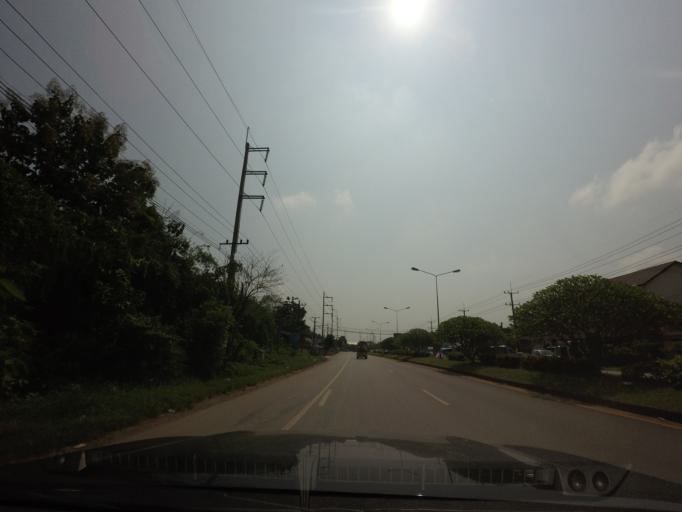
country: TH
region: Nan
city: Nan
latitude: 18.7867
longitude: 100.7425
